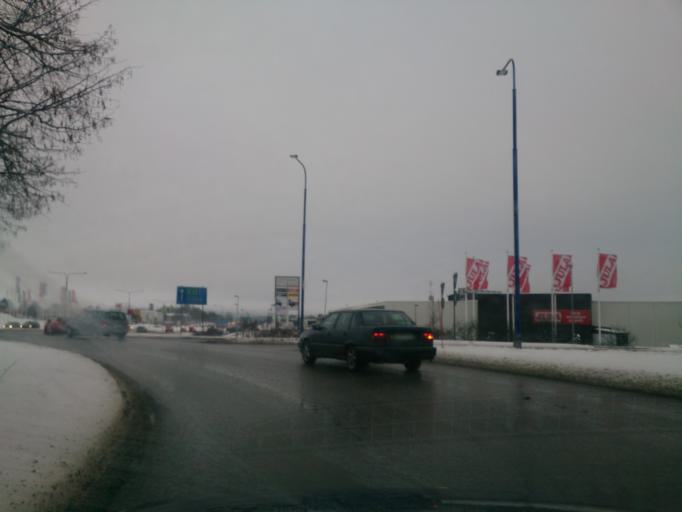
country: SE
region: OEstergoetland
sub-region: Norrkopings Kommun
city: Norrkoping
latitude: 58.6090
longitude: 16.1612
